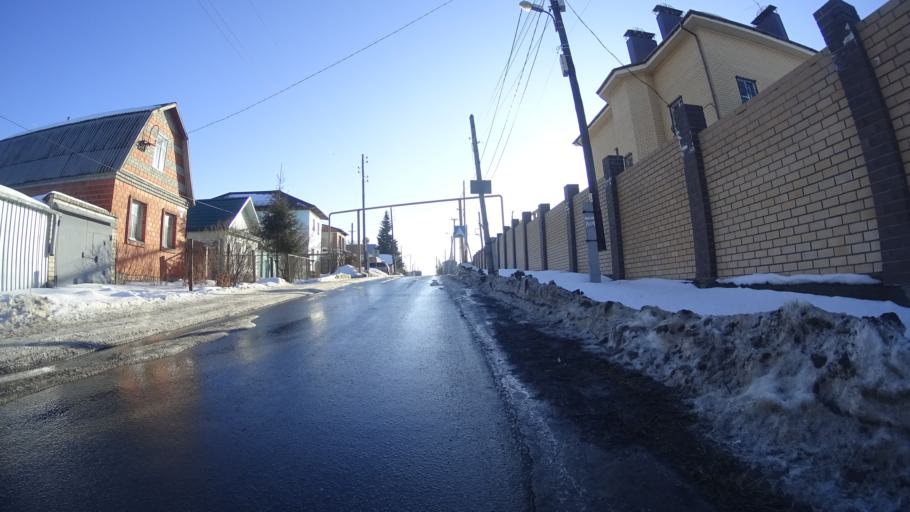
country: RU
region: Chelyabinsk
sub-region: Gorod Chelyabinsk
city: Chelyabinsk
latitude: 55.1535
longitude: 61.3102
